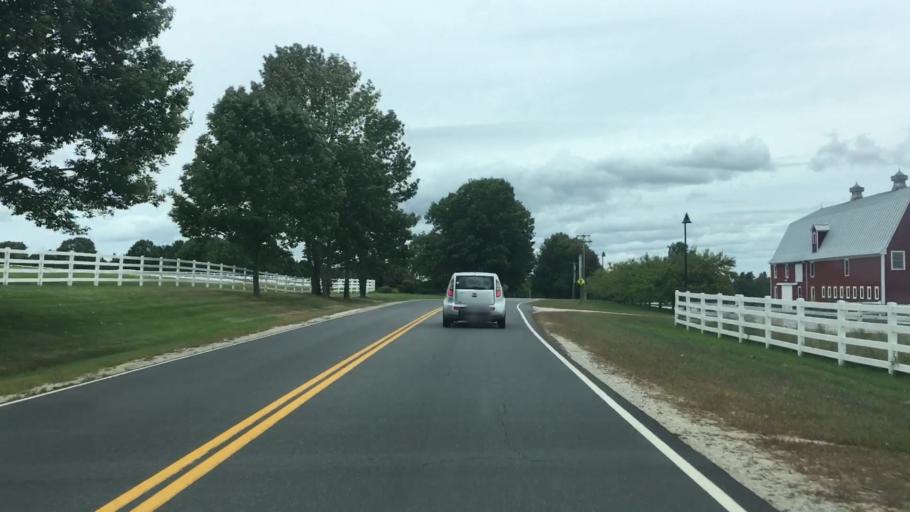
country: US
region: Maine
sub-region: Cumberland County
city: New Gloucester
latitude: 43.8939
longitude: -70.2544
